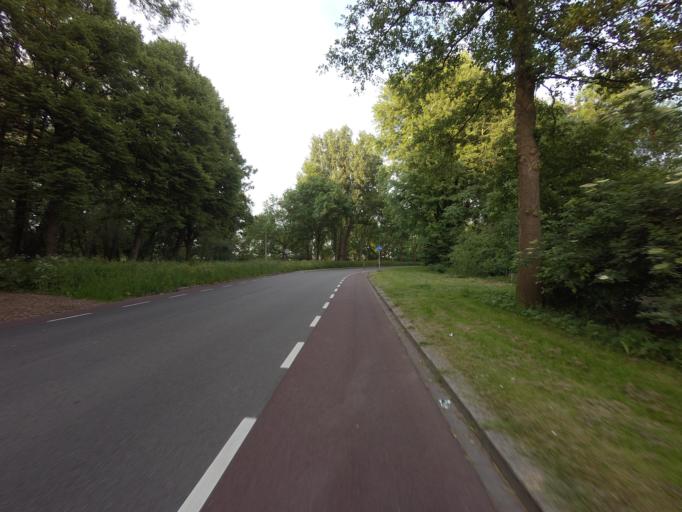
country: NL
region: South Holland
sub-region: Gemeente Gouda
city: Bloemendaal
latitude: 52.0388
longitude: 4.7071
